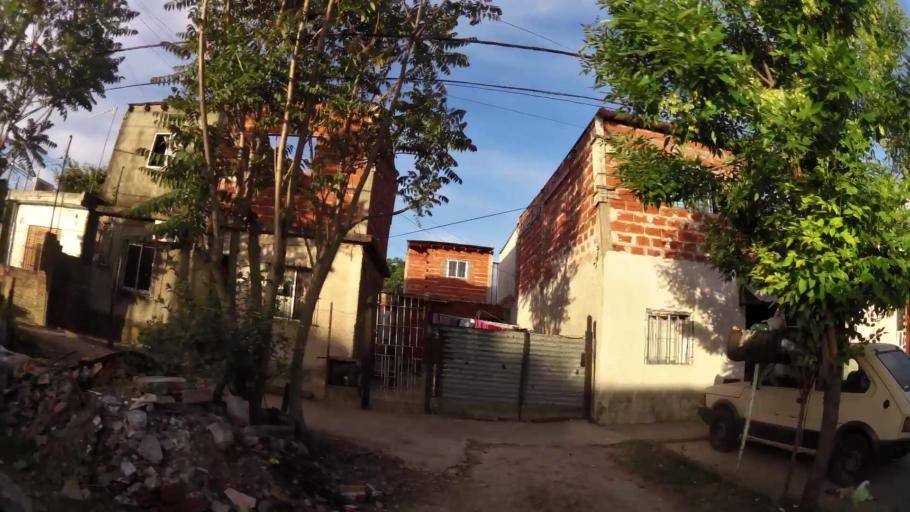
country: AR
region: Buenos Aires
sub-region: Partido de Quilmes
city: Quilmes
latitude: -34.7798
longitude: -58.1937
